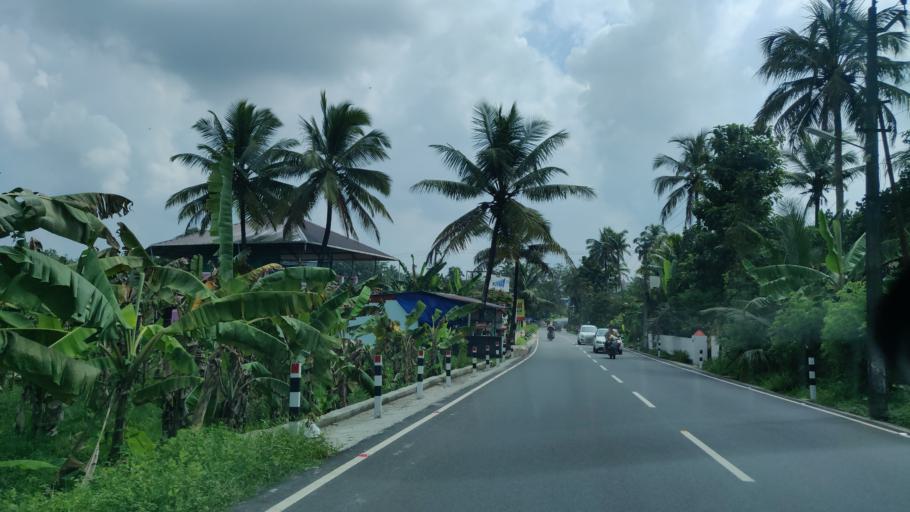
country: IN
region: Kerala
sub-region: Ernakulam
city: Angamali
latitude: 10.1681
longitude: 76.4199
